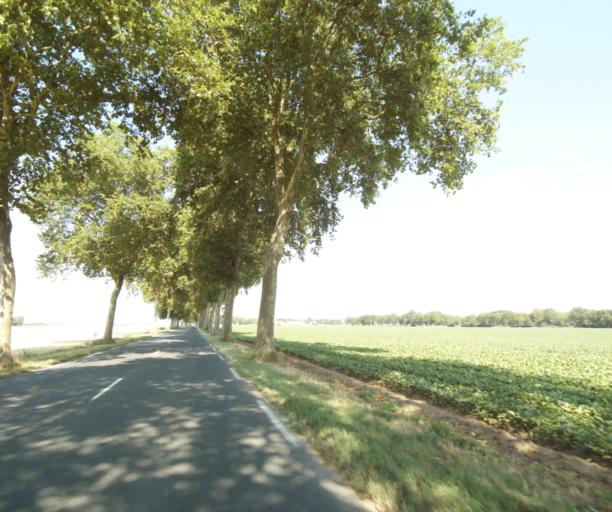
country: FR
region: Centre
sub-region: Departement du Loiret
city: Saint-Denis-en-Val
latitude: 47.8565
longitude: 1.9942
